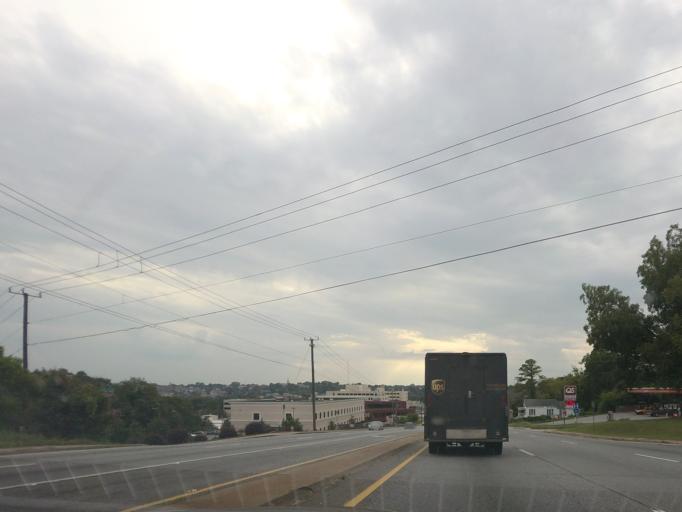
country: US
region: Georgia
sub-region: Bibb County
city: Macon
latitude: 32.8482
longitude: -83.6136
